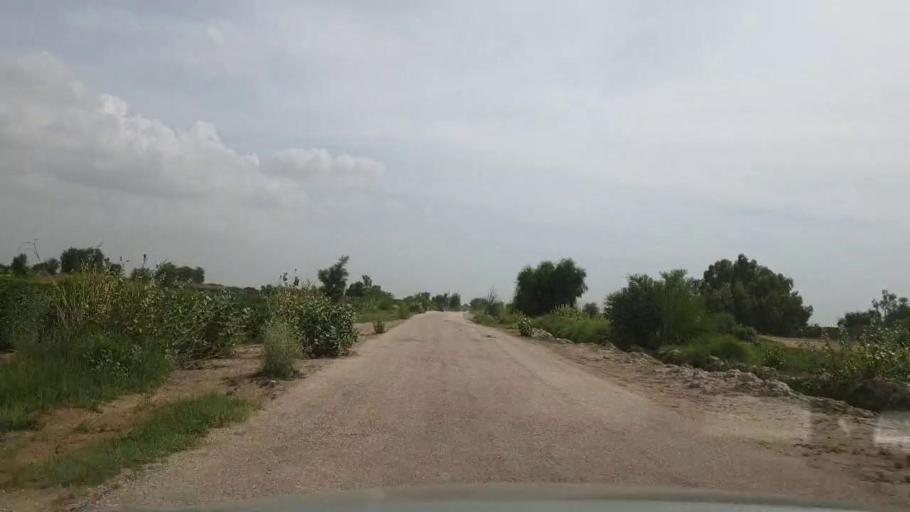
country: PK
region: Sindh
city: Kot Diji
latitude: 27.1280
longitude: 69.0284
